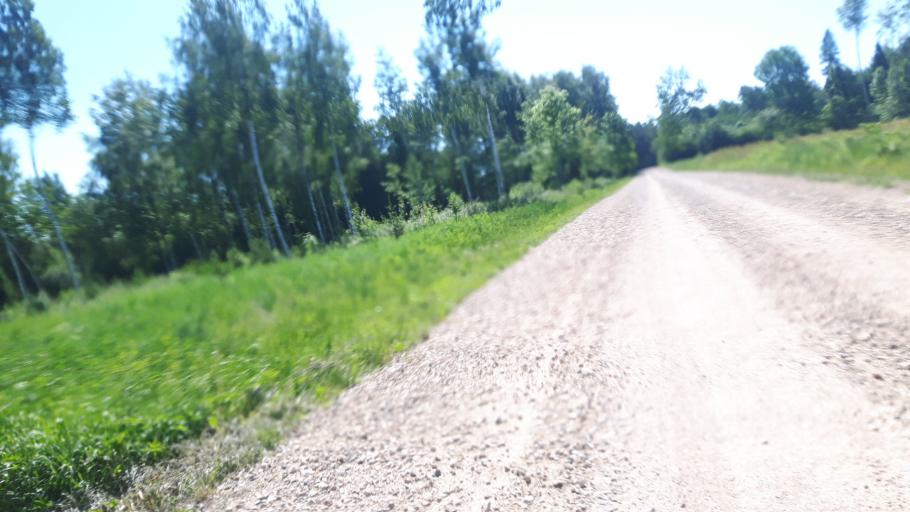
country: EE
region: Paernumaa
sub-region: Tootsi vald
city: Tootsi
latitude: 58.5116
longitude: 24.9089
